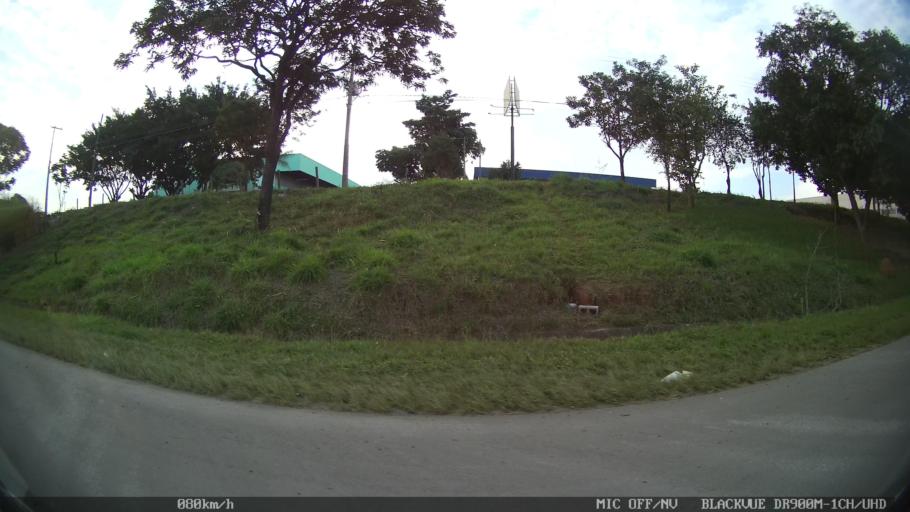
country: BR
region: Sao Paulo
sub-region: Americana
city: Americana
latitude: -22.6371
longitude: -47.3215
